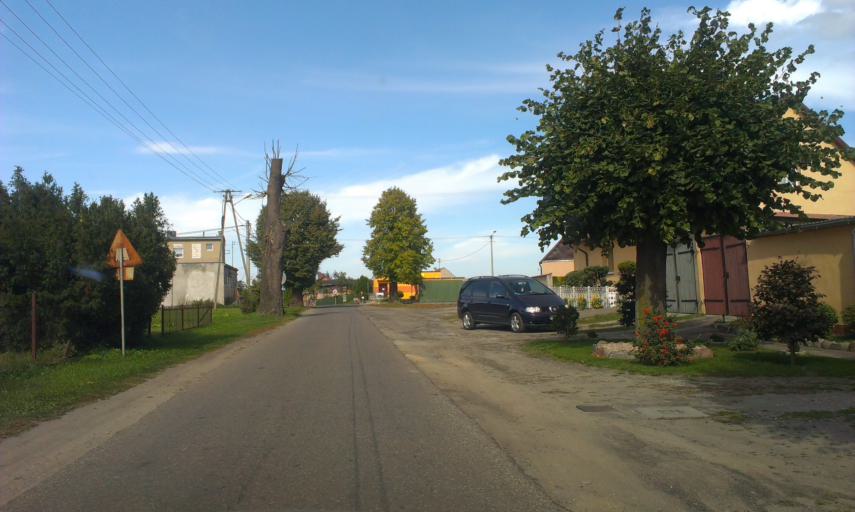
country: PL
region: Greater Poland Voivodeship
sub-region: Powiat zlotowski
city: Zlotow
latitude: 53.3050
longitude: 17.1294
